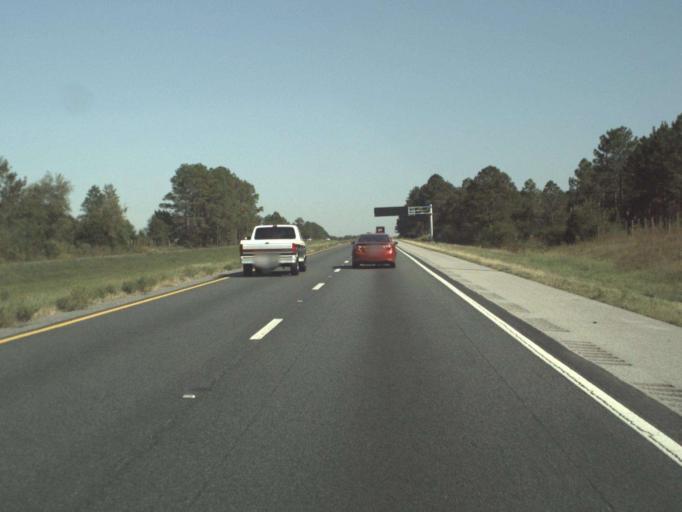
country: US
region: Florida
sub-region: Washington County
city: Chipley
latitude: 30.7510
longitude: -85.5737
